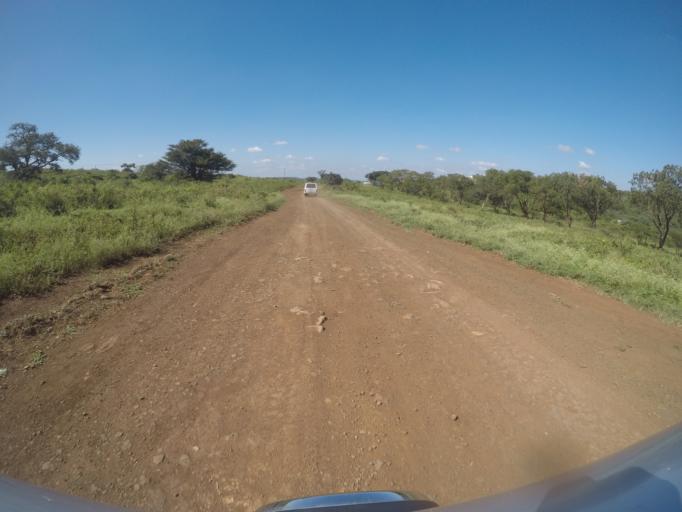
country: ZA
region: KwaZulu-Natal
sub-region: uThungulu District Municipality
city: Empangeni
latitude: -28.5634
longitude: 31.7020
